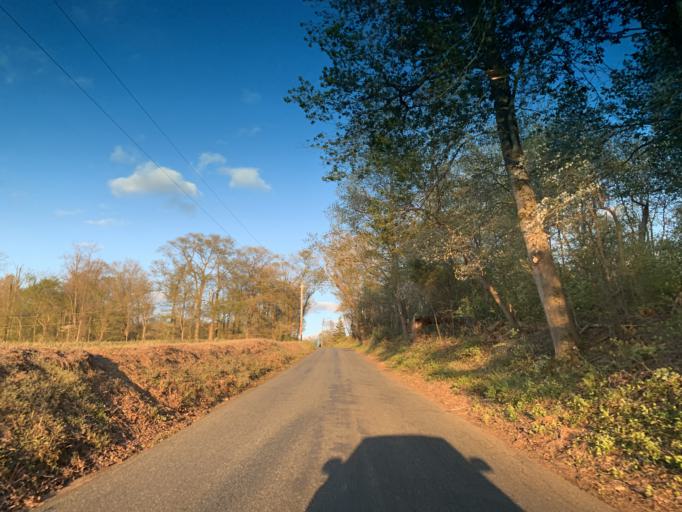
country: US
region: Maryland
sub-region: Harford County
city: Jarrettsville
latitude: 39.6563
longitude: -76.4315
